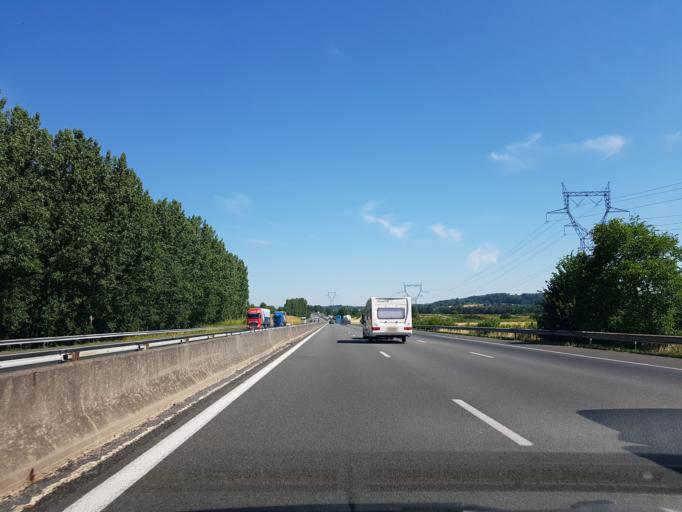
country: FR
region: Picardie
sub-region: Departement de l'Oise
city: Longueil-Sainte-Marie
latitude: 49.3687
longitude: 2.7041
